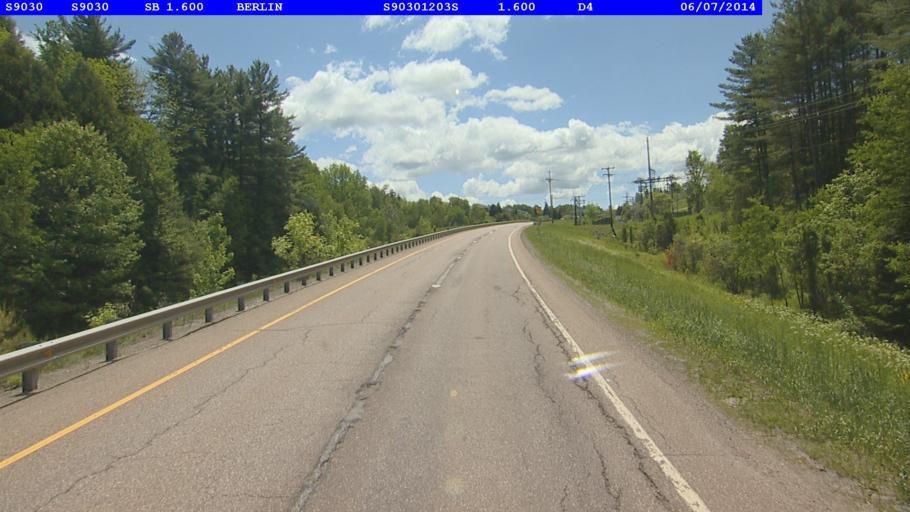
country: US
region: Vermont
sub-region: Washington County
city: Montpelier
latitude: 44.2231
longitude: -72.5578
